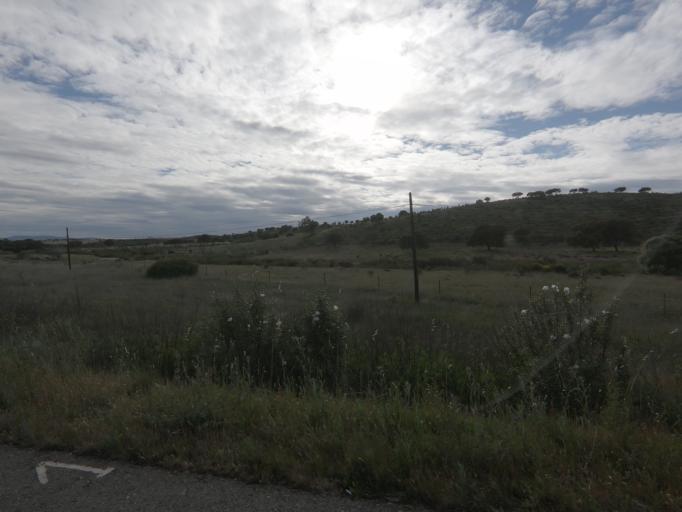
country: ES
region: Extremadura
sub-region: Provincia de Caceres
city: Perales del Puerto
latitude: 40.1157
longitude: -6.6703
